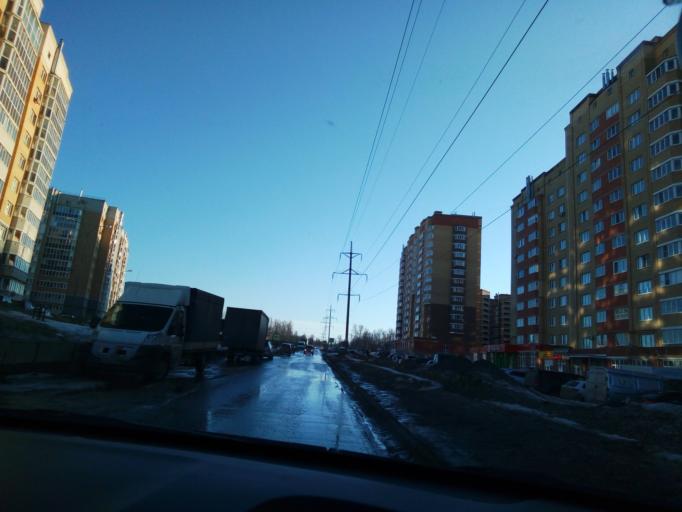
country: RU
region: Chuvashia
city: Novyye Lapsary
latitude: 56.1338
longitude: 47.1550
